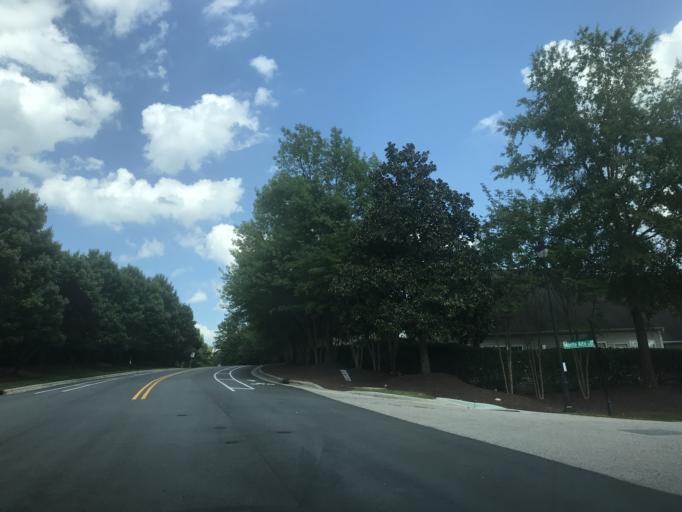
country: US
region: North Carolina
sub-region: Wake County
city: Cary
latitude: 35.8875
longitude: -78.7294
